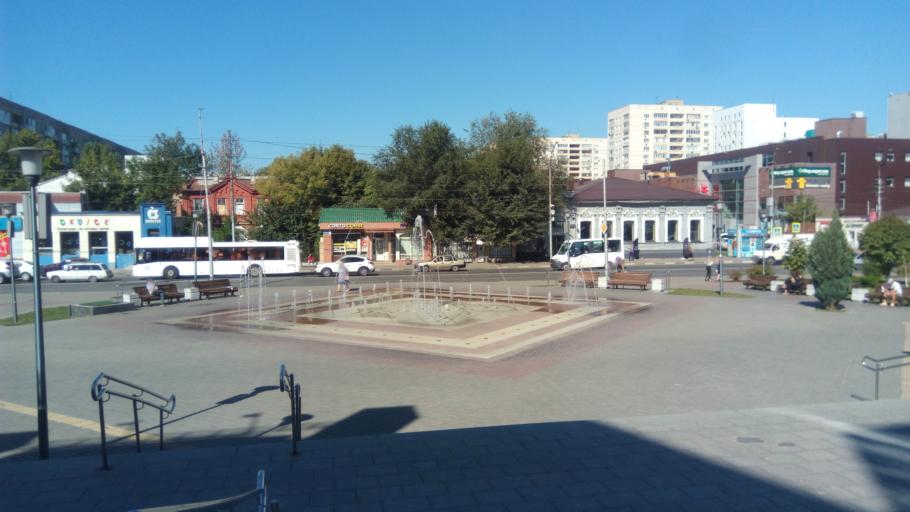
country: RU
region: Saratov
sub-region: Saratovskiy Rayon
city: Saratov
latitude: 51.5348
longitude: 46.0233
